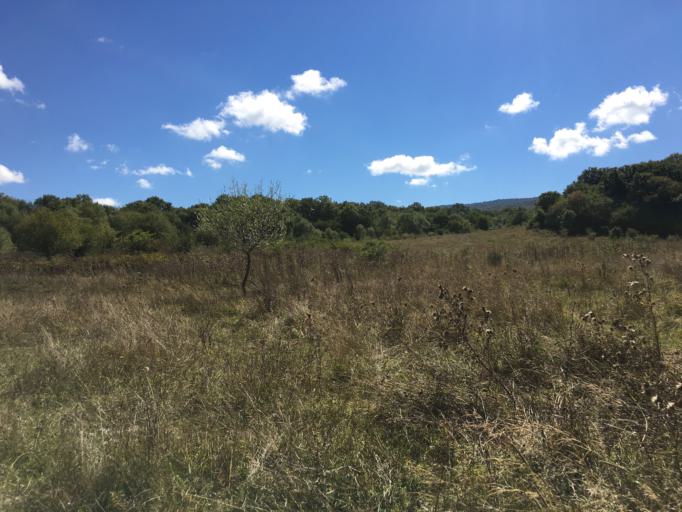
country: GE
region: Mtskheta-Mtianeti
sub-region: Tianetis Munitsip'alit'et'i
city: T'ianet'i
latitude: 41.9374
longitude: 44.9747
